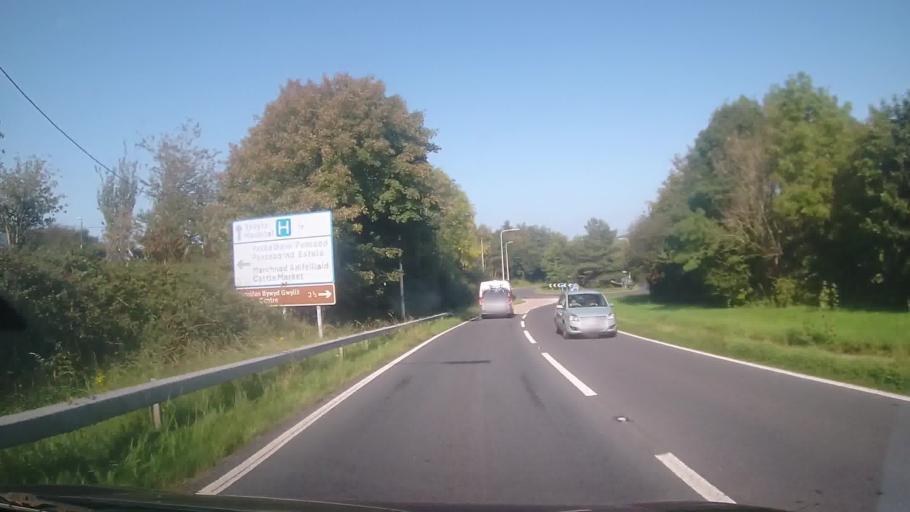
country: GB
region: Wales
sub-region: County of Ceredigion
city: Cardigan
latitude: 52.0753
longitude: -4.6571
